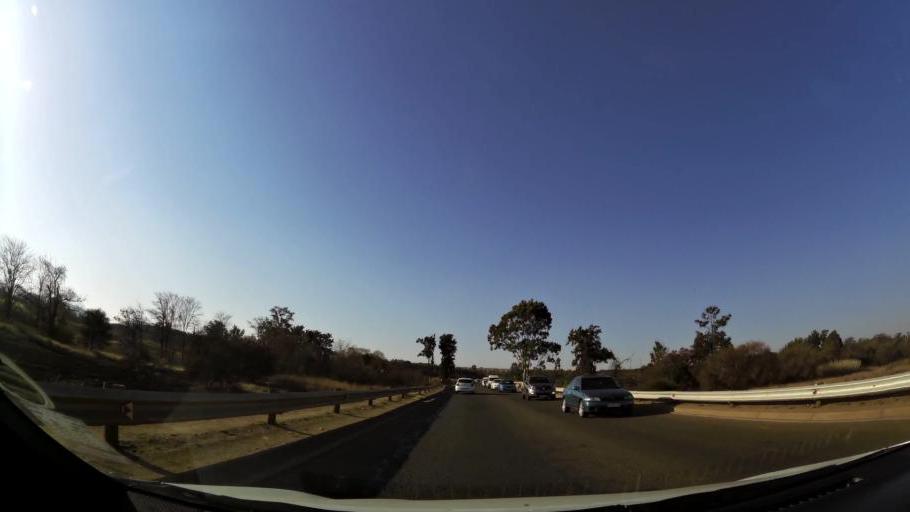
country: ZA
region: Gauteng
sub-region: City of Tshwane Metropolitan Municipality
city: Cullinan
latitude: -25.7472
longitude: 28.3714
